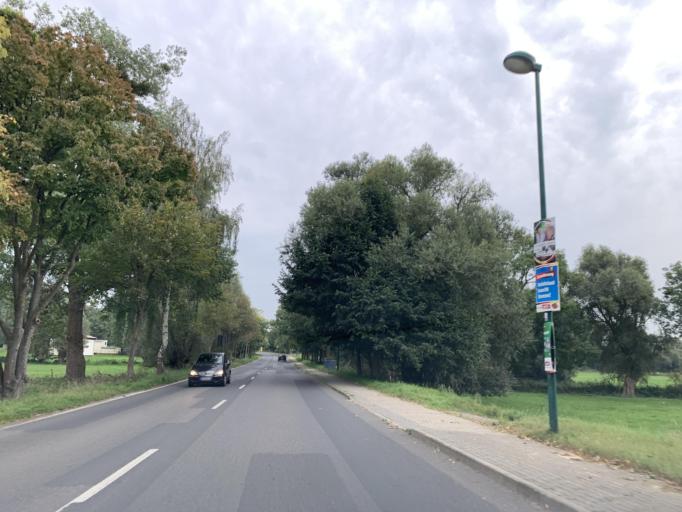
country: DE
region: Brandenburg
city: Mittenwalde
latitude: 53.3321
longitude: 13.7030
